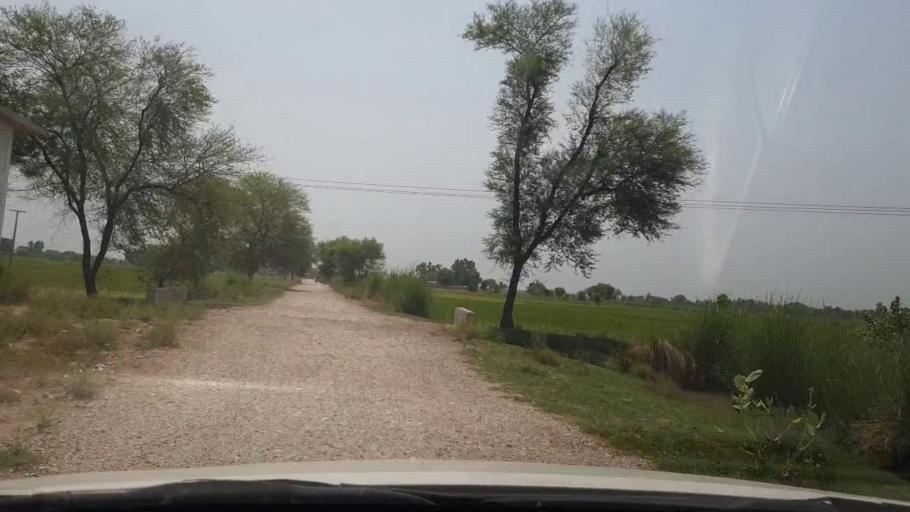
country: PK
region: Sindh
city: Rustam jo Goth
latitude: 28.0093
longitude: 68.7672
